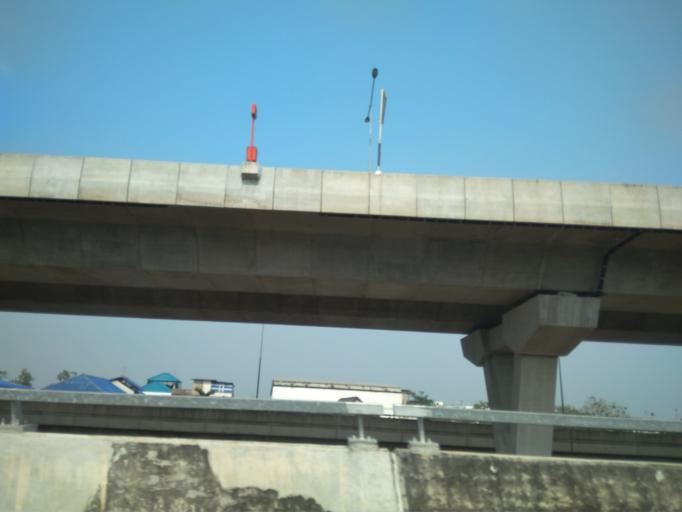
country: TH
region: Bangkok
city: Taling Chan
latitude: 13.7957
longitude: 100.4318
